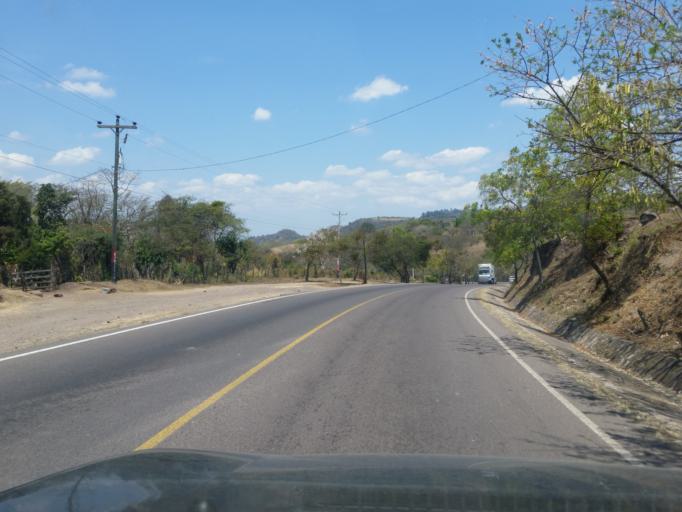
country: NI
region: Esteli
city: Esteli
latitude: 13.0315
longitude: -86.3191
